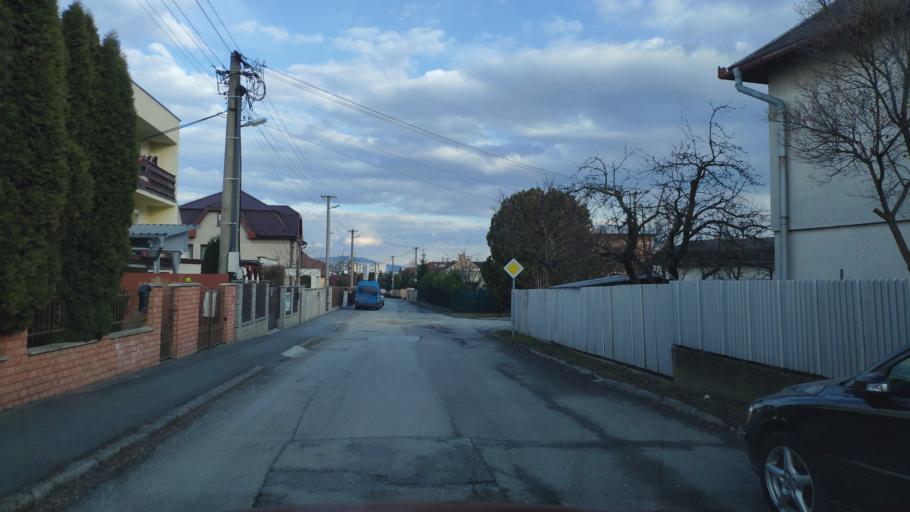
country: SK
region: Kosicky
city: Kosice
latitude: 48.6835
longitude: 21.2620
